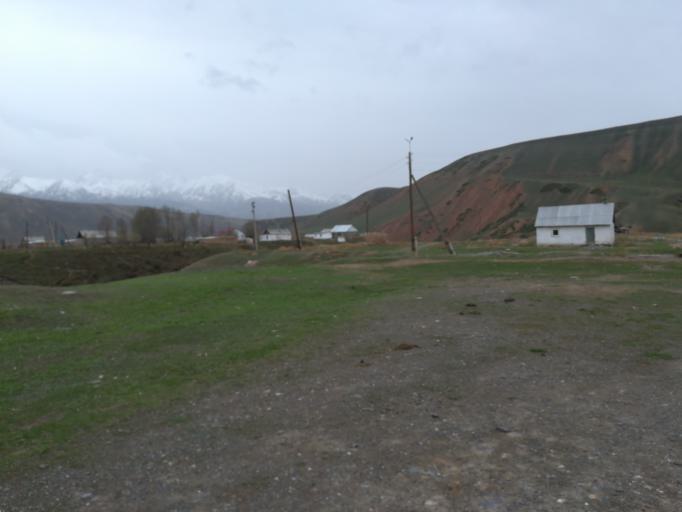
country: KG
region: Naryn
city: Naryn
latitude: 41.5164
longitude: 76.4361
